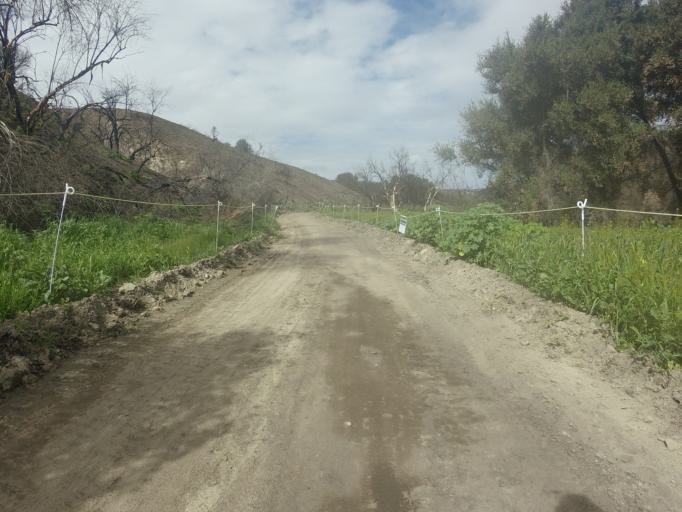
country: US
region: California
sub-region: Orange County
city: Aliso Viejo
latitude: 33.5488
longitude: -117.7417
